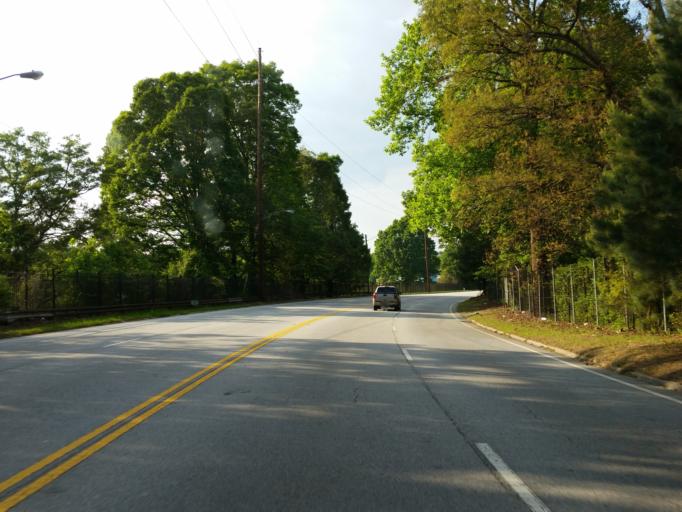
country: US
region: Georgia
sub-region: Cobb County
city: Vinings
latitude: 33.7804
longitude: -84.4765
